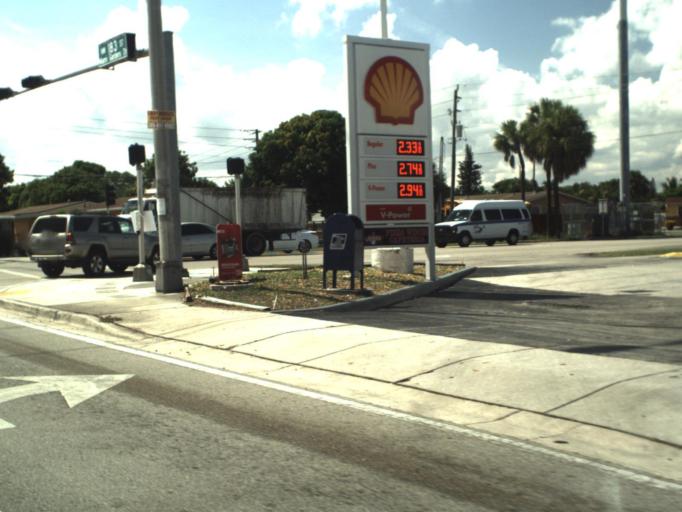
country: US
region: Florida
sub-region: Miami-Dade County
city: Carol City
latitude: 25.9401
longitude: -80.2691
